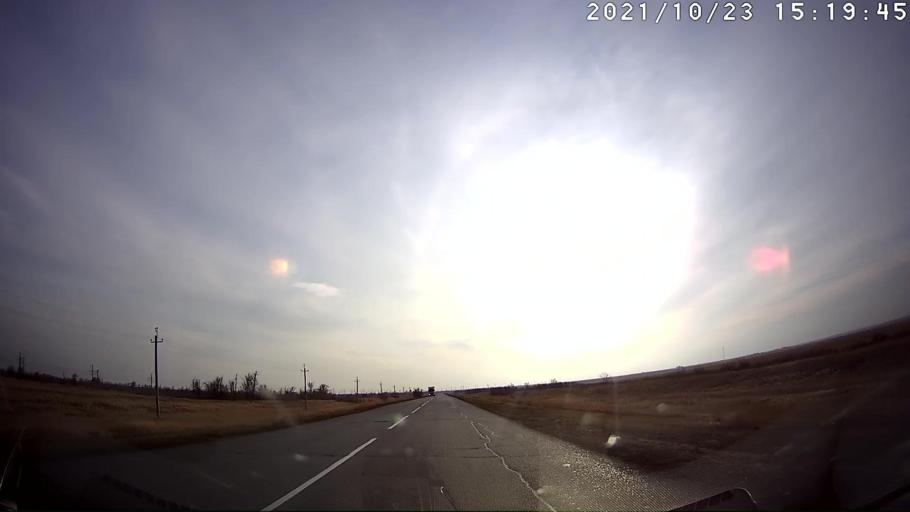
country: RU
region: Volgograd
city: Bereslavka
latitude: 48.3266
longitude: 44.3310
